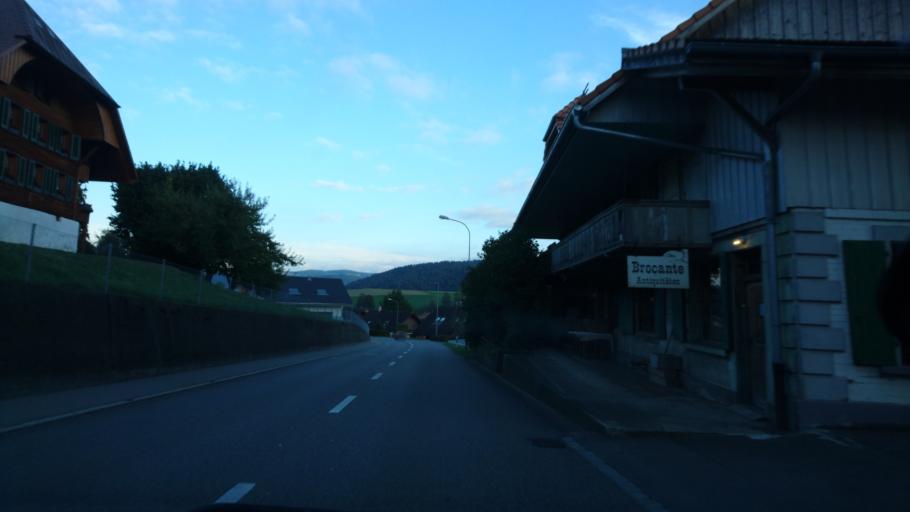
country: CH
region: Bern
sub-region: Bern-Mittelland District
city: Zaziwil
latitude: 46.9024
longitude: 7.6564
